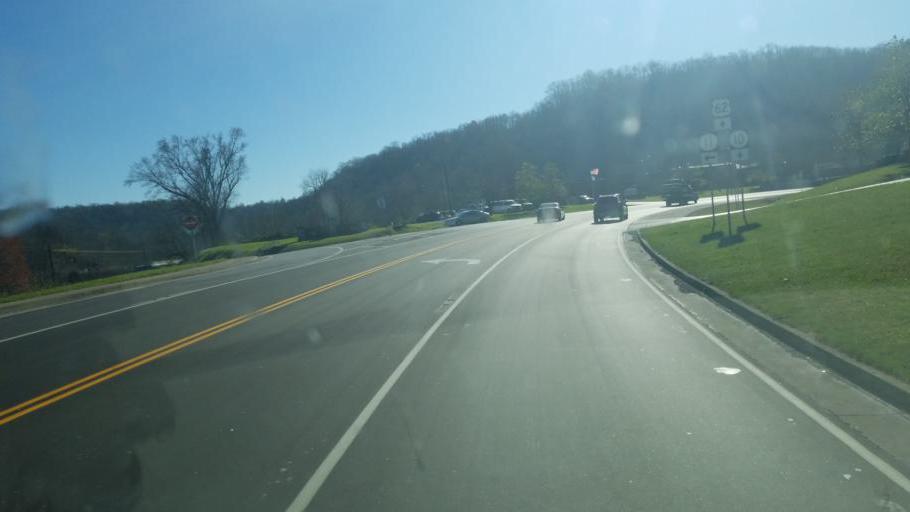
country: US
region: Kentucky
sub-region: Mason County
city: Maysville
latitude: 38.6401
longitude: -83.7569
